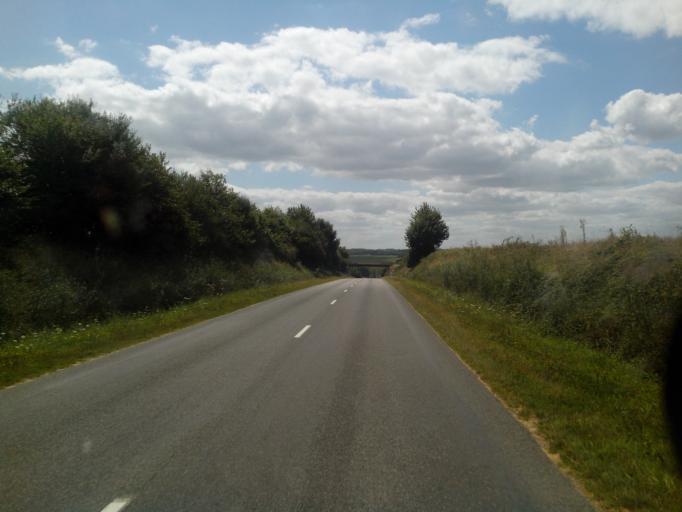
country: FR
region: Brittany
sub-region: Departement des Cotes-d'Armor
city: Plumieux
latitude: 48.0955
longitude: -2.5373
